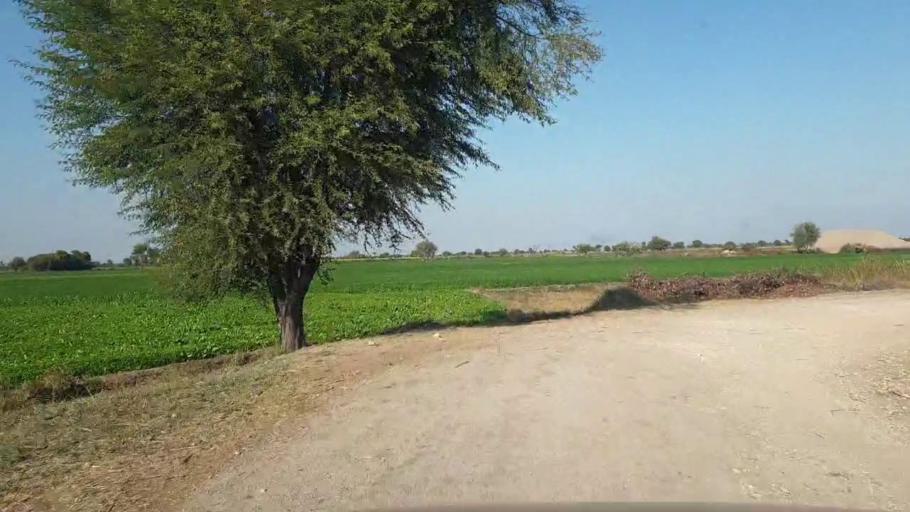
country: PK
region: Sindh
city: Shahpur Chakar
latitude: 26.1616
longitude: 68.6848
